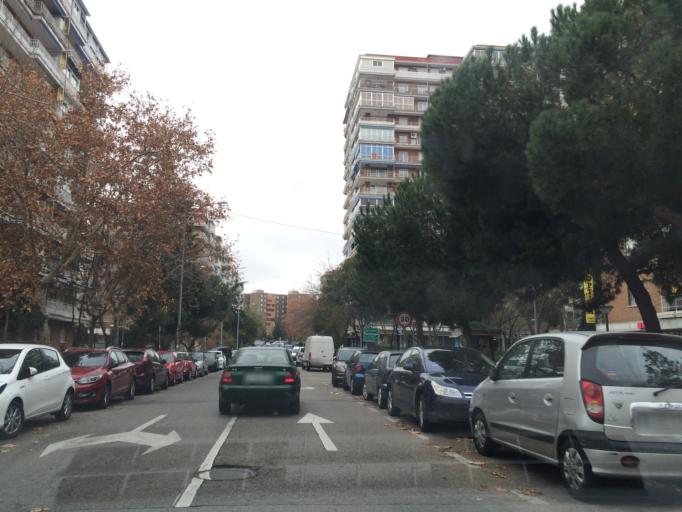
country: ES
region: Madrid
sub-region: Provincia de Madrid
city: Alcorcon
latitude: 40.3520
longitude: -3.8189
